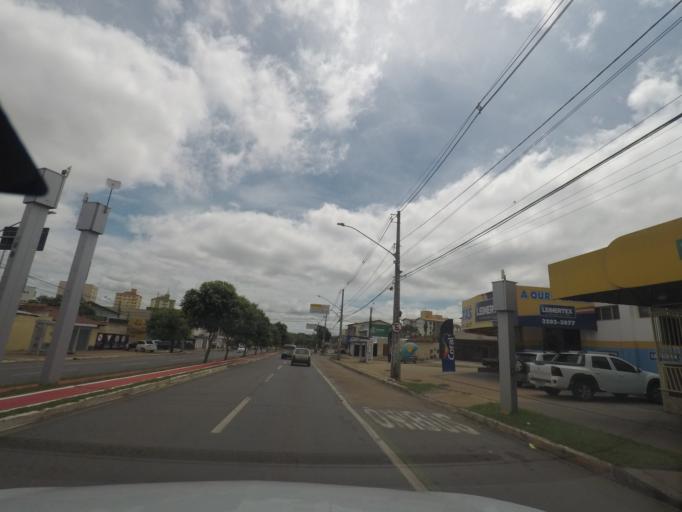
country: BR
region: Goias
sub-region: Goiania
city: Goiania
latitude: -16.6736
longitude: -49.2357
